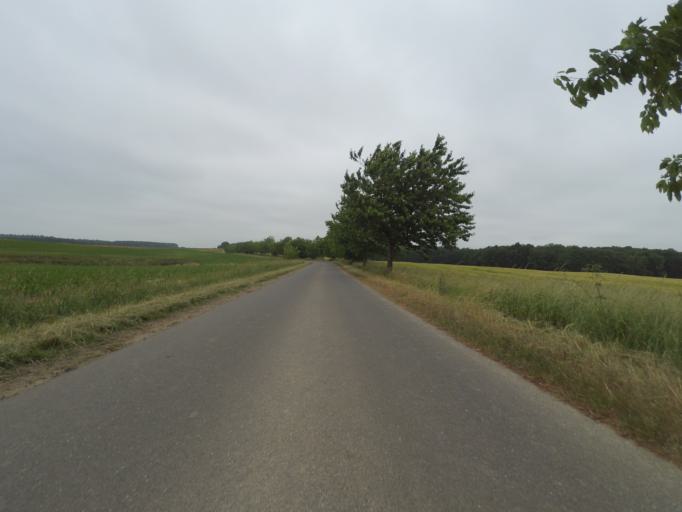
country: DE
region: Mecklenburg-Vorpommern
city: Goldberg
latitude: 53.5571
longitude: 12.0258
